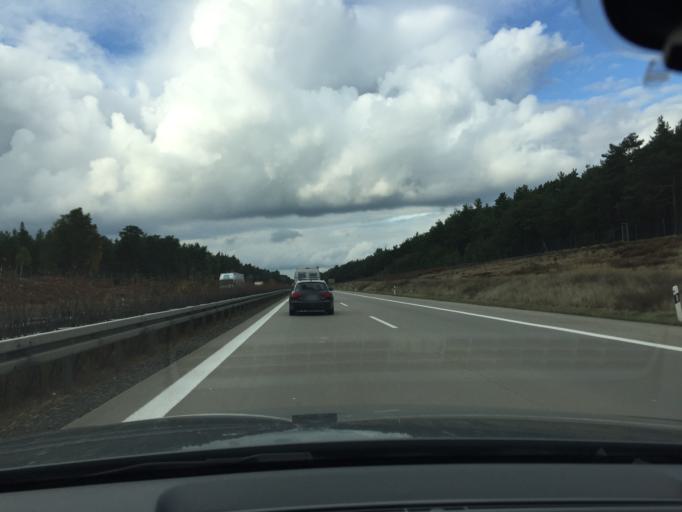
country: DE
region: Brandenburg
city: Kasel-Golzig
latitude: 51.9201
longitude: 13.7817
